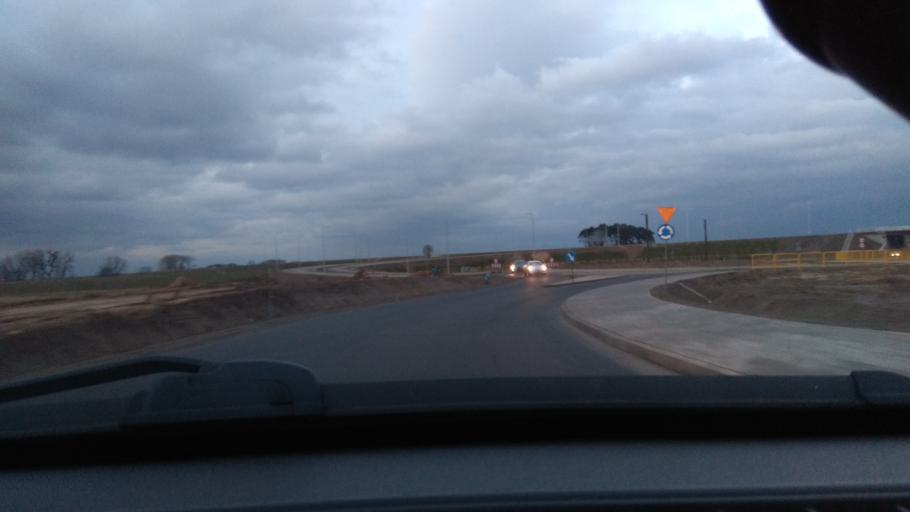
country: PL
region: Greater Poland Voivodeship
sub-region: Powiat kepinski
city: Baranow
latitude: 51.2892
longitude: 18.0196
